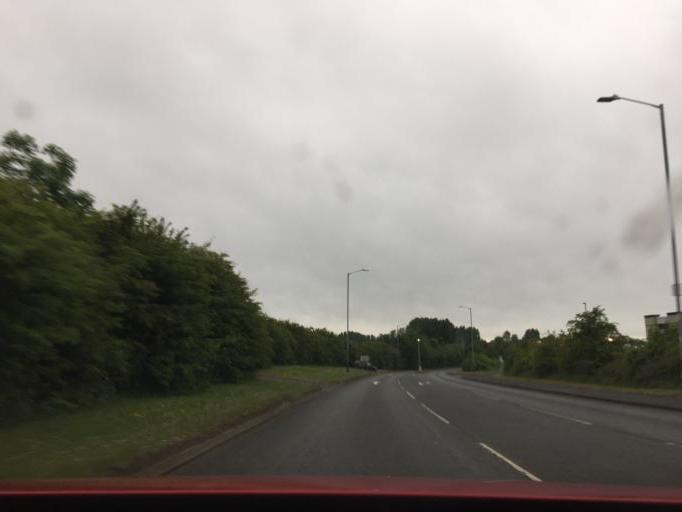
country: GB
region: England
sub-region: Warwickshire
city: Attleborough
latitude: 52.5228
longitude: -1.4378
